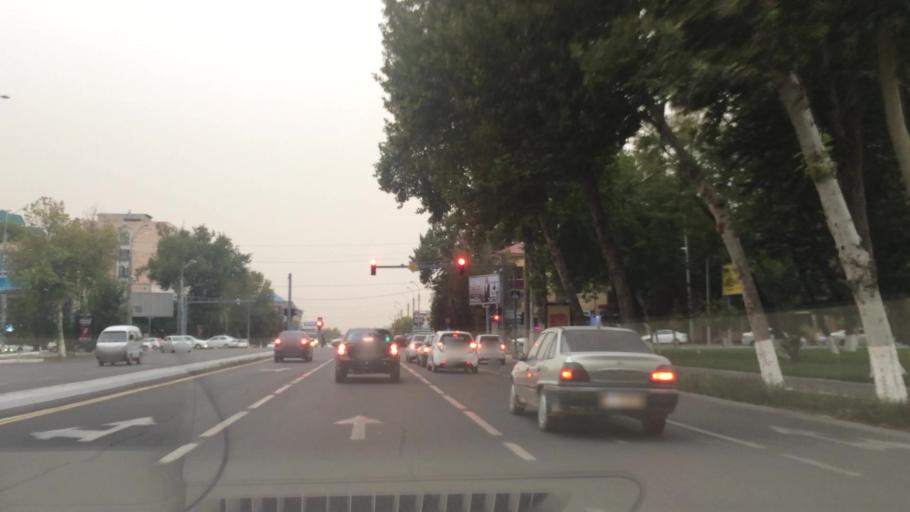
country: UZ
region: Toshkent Shahri
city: Tashkent
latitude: 41.3017
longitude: 69.2773
